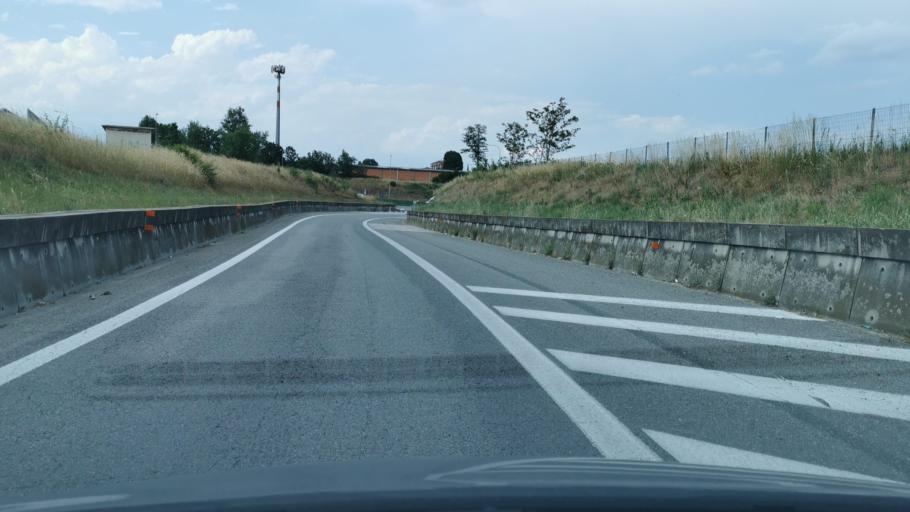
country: IT
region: Piedmont
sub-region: Provincia di Torino
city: Venaria Reale
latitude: 45.1192
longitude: 7.6406
